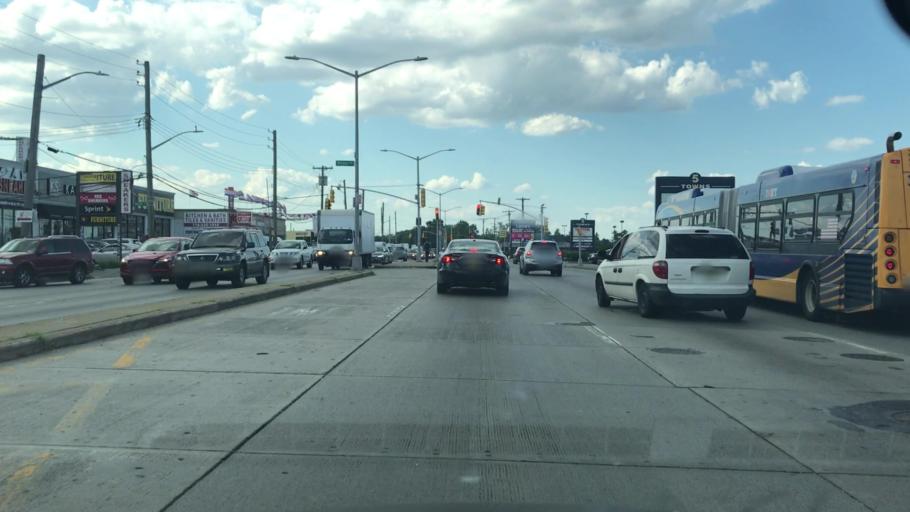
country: US
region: New York
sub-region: Nassau County
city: Inwood
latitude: 40.6358
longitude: -73.7401
